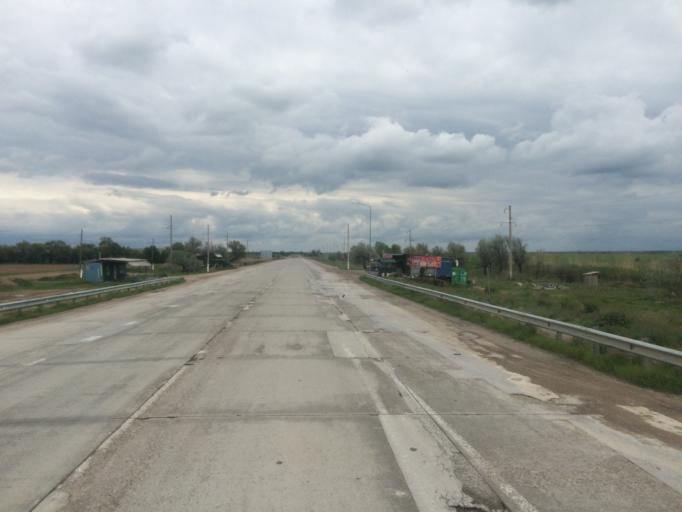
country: KG
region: Chuy
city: Sokuluk
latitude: 43.2716
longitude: 74.2394
